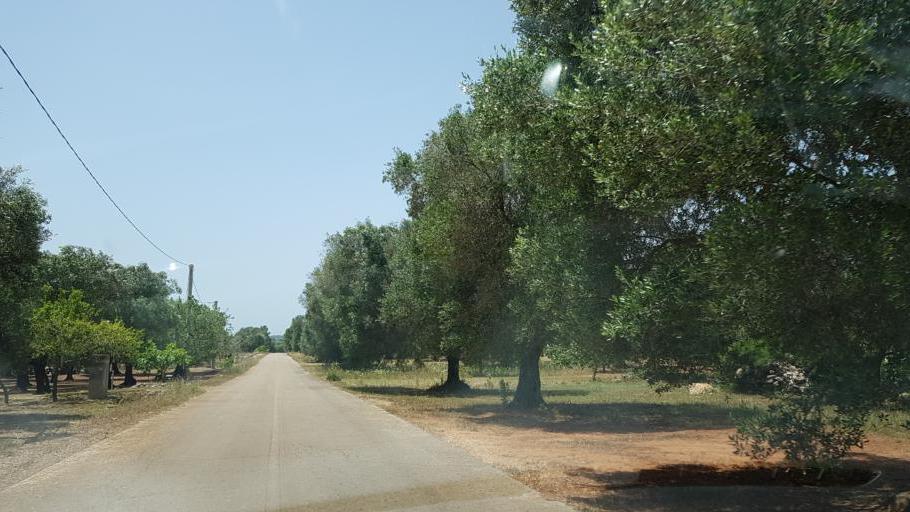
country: IT
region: Apulia
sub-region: Provincia di Lecce
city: Porto Cesareo
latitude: 40.3243
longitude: 17.8899
